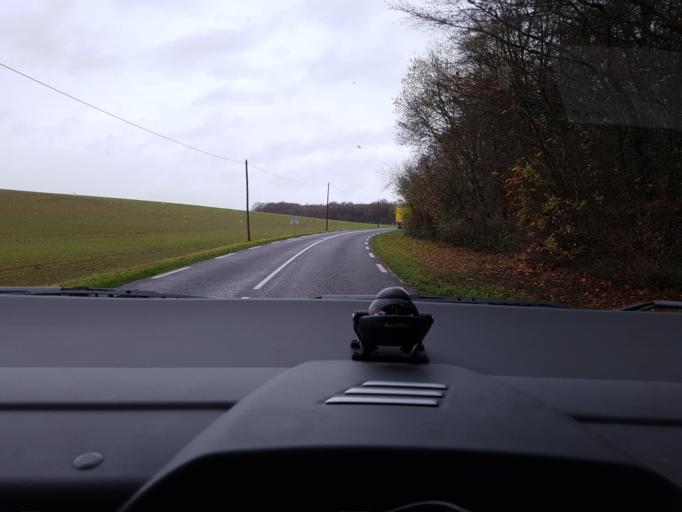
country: FR
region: Haute-Normandie
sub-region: Departement de la Seine-Maritime
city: Gournay-en-Bray
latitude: 49.4256
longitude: 1.6434
